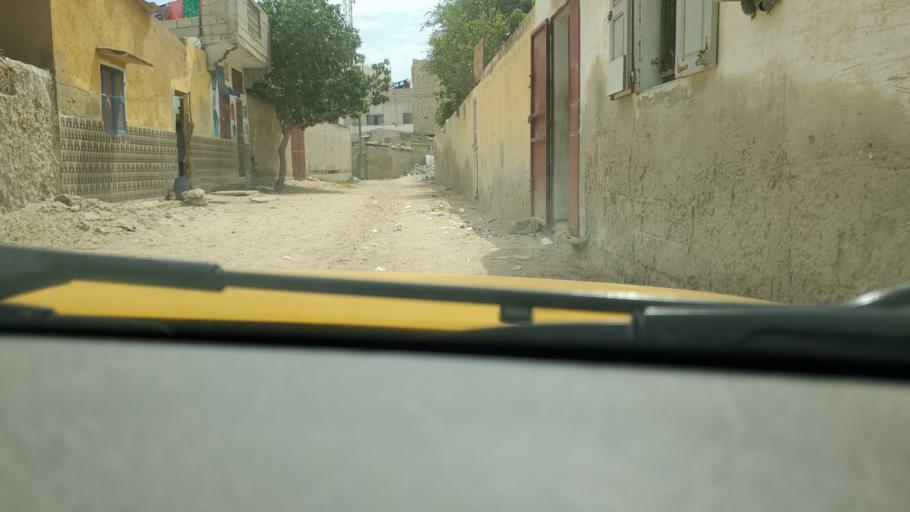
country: SN
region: Saint-Louis
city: Saint-Louis
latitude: 16.0259
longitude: -16.4739
